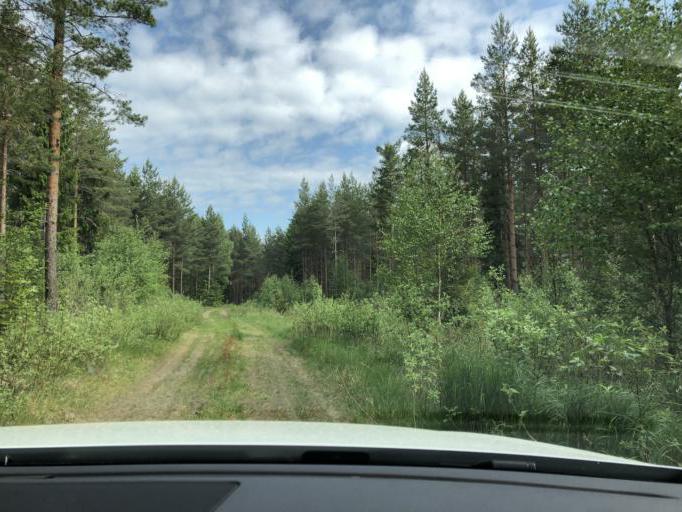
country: SE
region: Dalarna
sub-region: Avesta Kommun
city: Horndal
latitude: 60.2201
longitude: 16.5055
